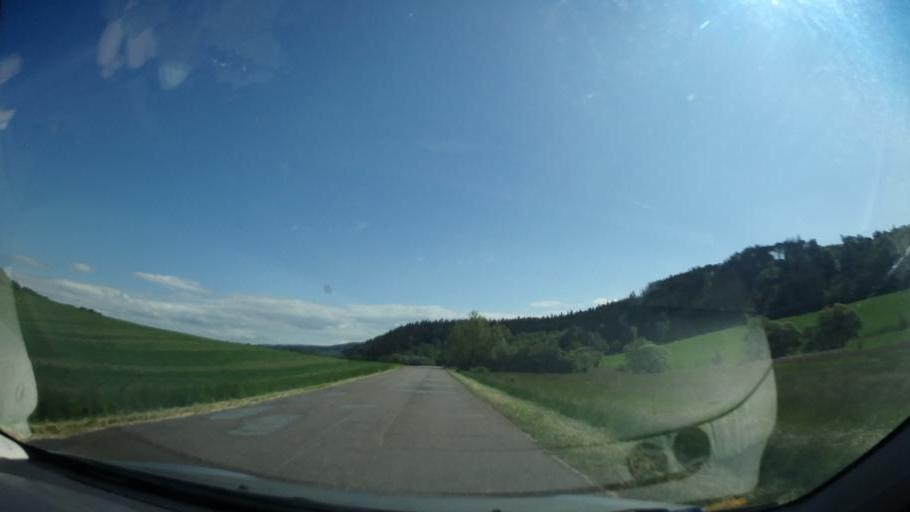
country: CZ
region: South Moravian
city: Velke Opatovice
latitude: 49.6371
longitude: 16.6106
